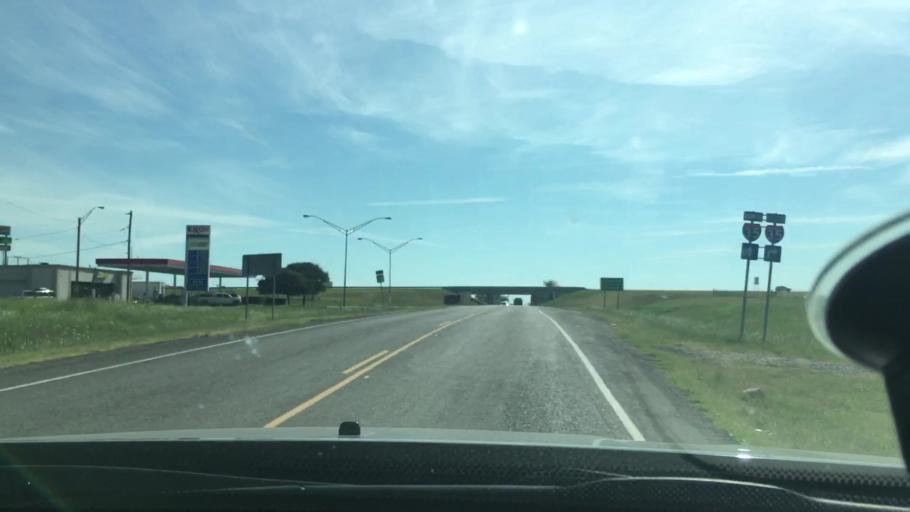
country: US
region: Oklahoma
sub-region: Carter County
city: Ardmore
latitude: 34.3327
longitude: -97.1561
